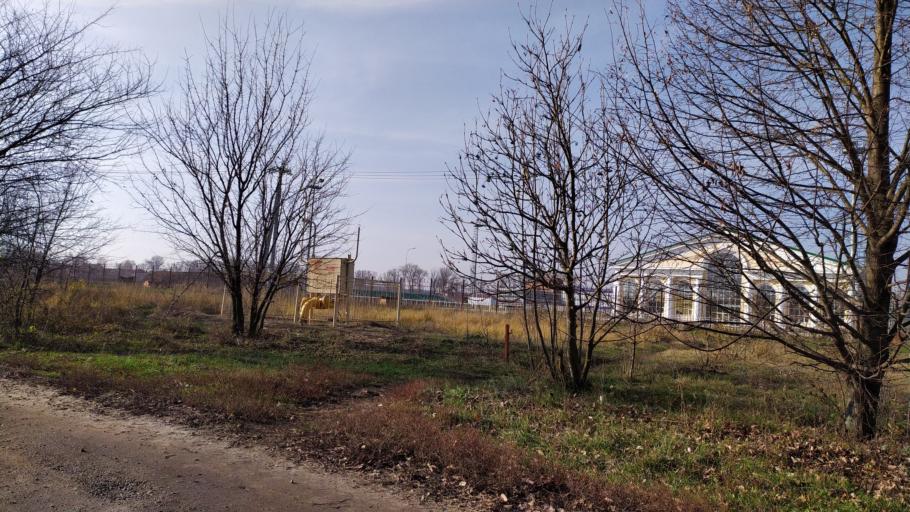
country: RU
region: Kursk
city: Kursk
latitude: 51.6415
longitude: 36.1310
